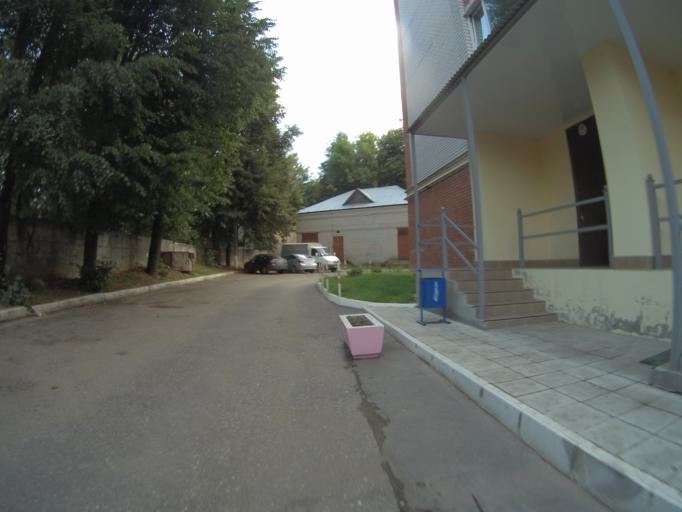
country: RU
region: Vladimir
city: Vladimir
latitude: 56.1342
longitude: 40.3664
